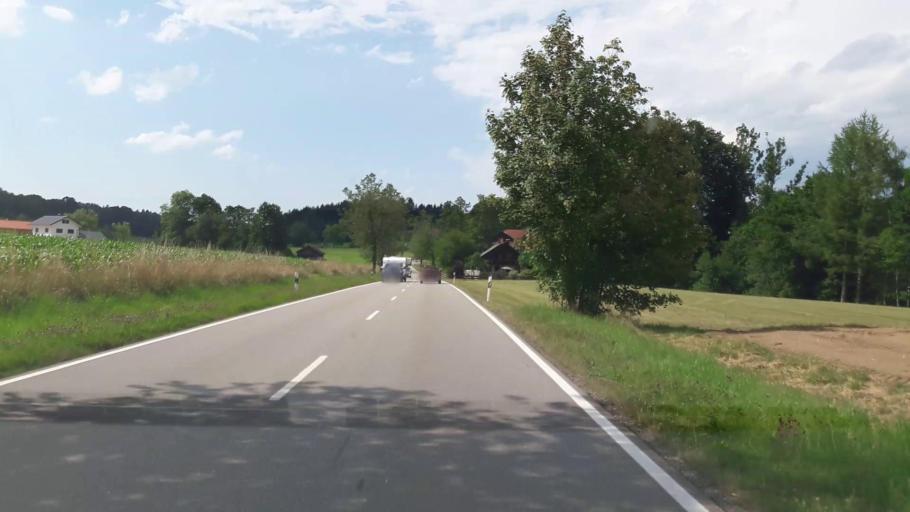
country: DE
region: Bavaria
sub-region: Upper Bavaria
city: Anger
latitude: 47.8040
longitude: 12.8631
